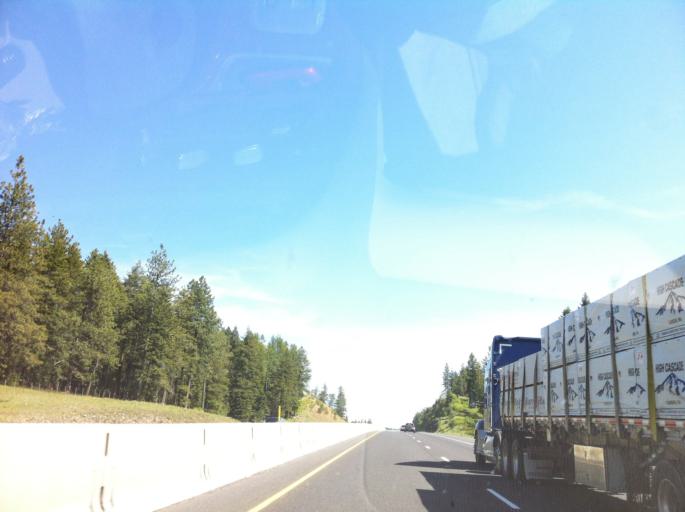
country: US
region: Oregon
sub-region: Umatilla County
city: Mission
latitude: 45.4822
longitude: -118.4040
